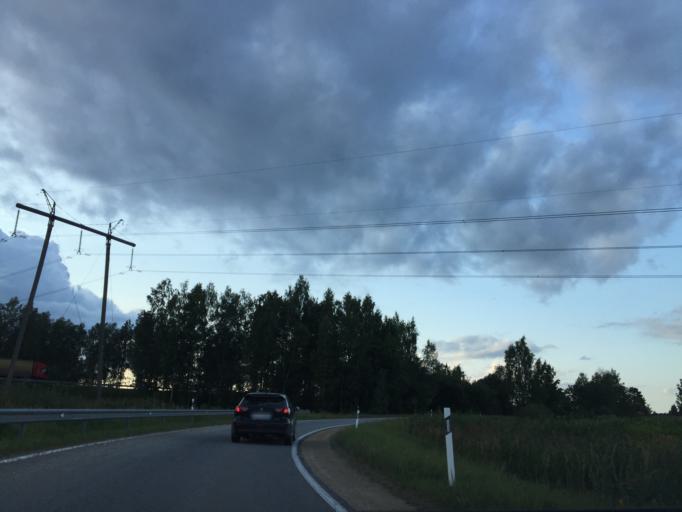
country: LV
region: Salaspils
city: Salaspils
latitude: 56.8468
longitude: 24.3993
